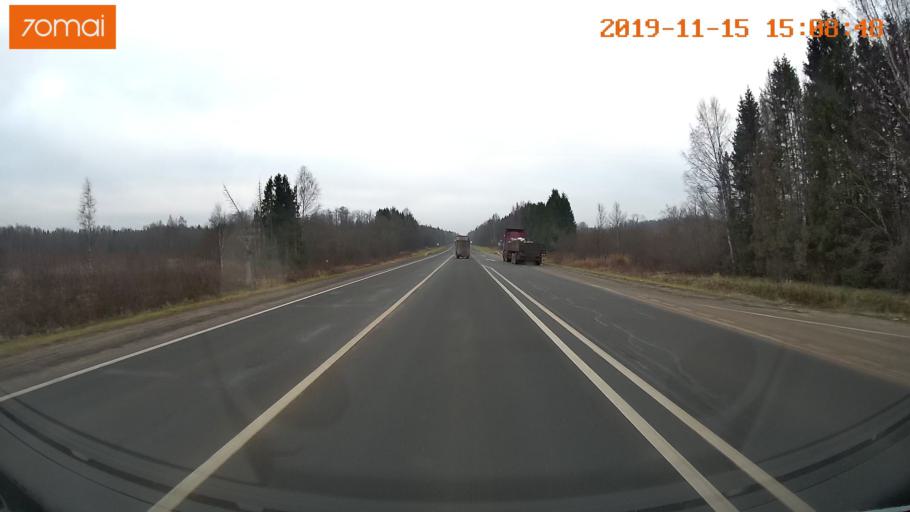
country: RU
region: Jaroslavl
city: Prechistoye
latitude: 58.3658
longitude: 40.2720
